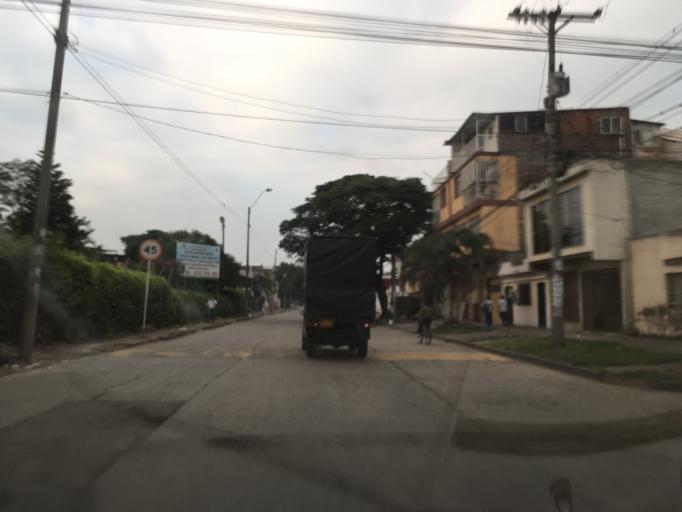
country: CO
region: Valle del Cauca
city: Cali
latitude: 3.4226
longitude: -76.5216
